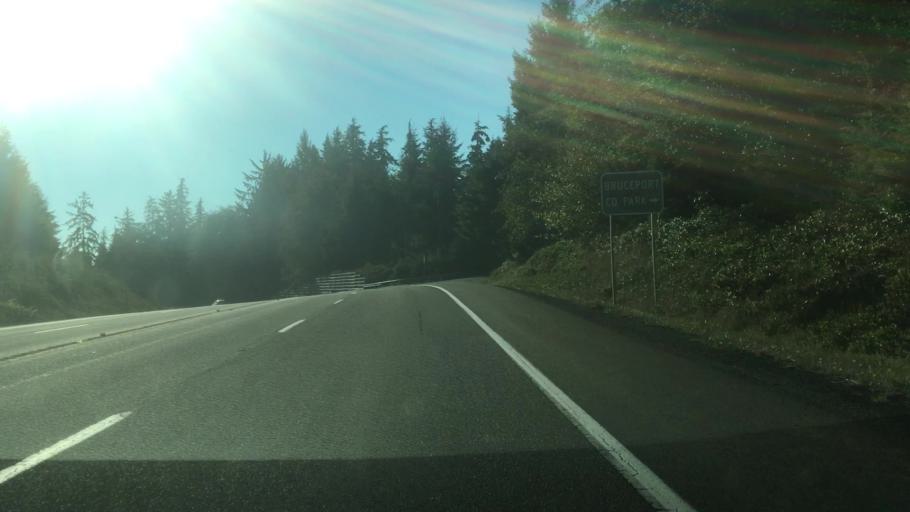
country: US
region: Washington
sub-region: Pacific County
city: South Bend
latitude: 46.6830
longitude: -123.8907
